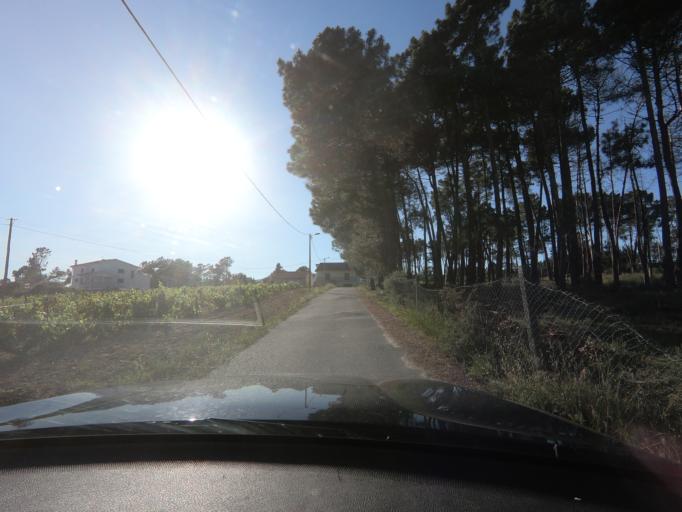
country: PT
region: Vila Real
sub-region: Vila Real
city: Vila Real
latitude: 41.3161
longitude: -7.6872
